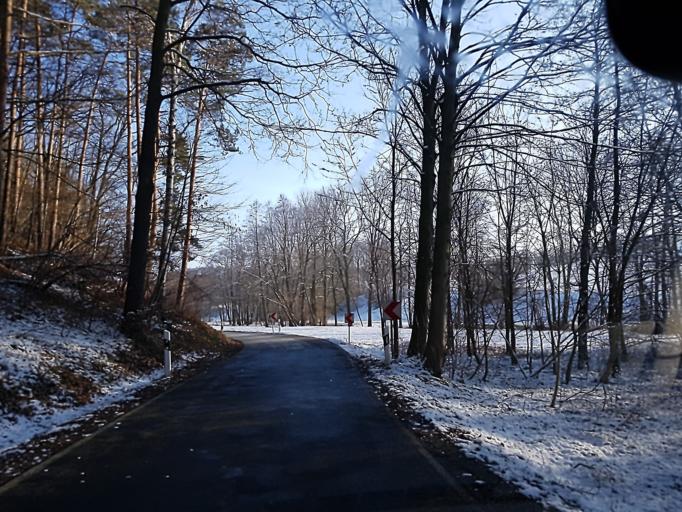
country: DE
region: Saxony
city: Leisnig
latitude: 51.1481
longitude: 12.9753
